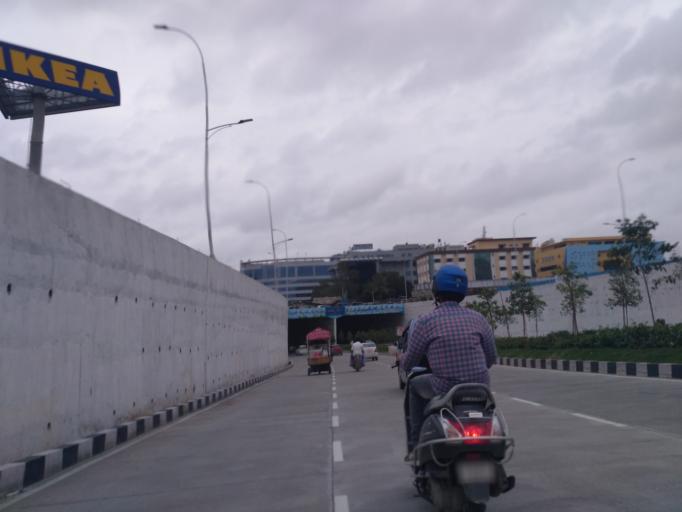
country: IN
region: Telangana
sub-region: Rangareddi
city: Kukatpalli
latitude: 17.4386
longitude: 78.3762
